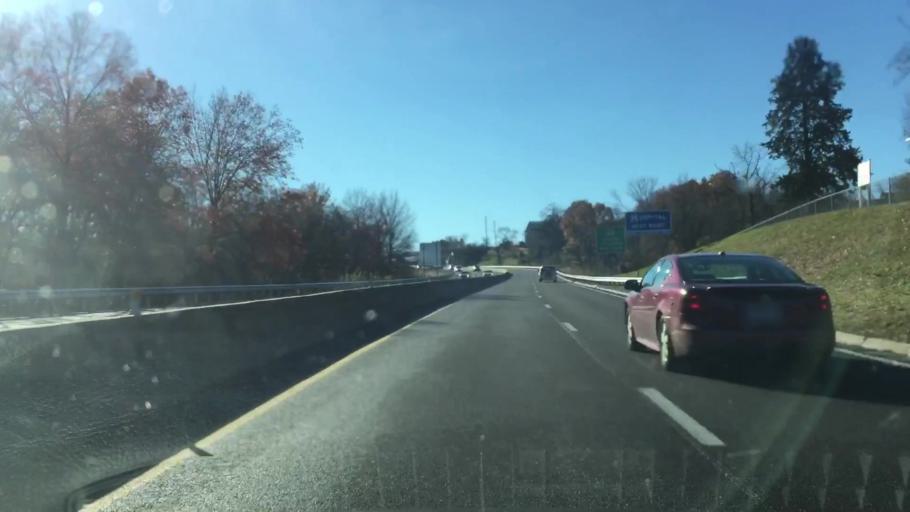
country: US
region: Missouri
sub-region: Cole County
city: Jefferson City
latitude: 38.5704
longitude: -92.1839
